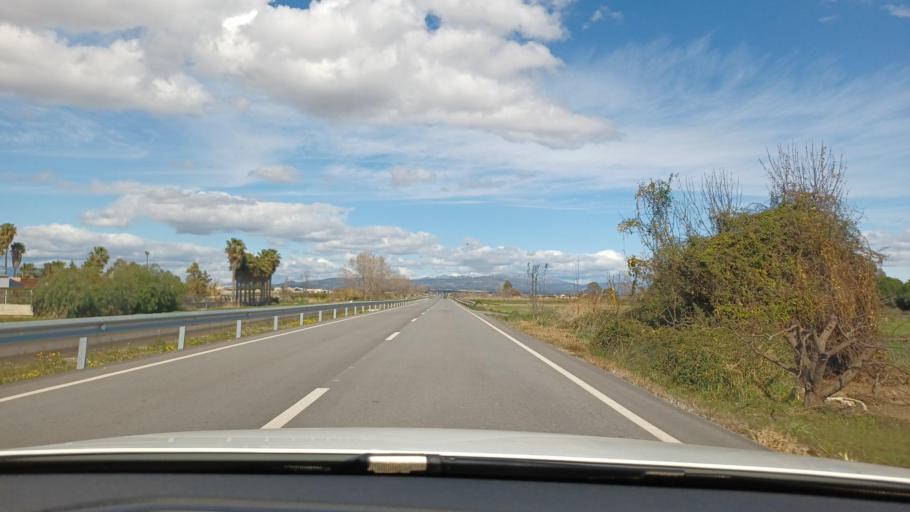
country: ES
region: Catalonia
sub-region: Provincia de Tarragona
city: Amposta
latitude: 40.6757
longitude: 0.5906
